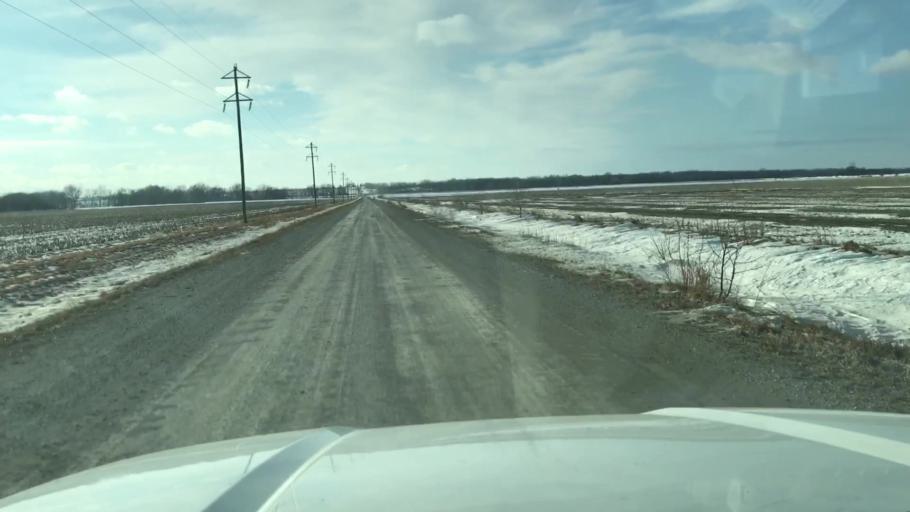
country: US
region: Missouri
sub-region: Holt County
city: Oregon
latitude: 40.1300
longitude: -95.0275
